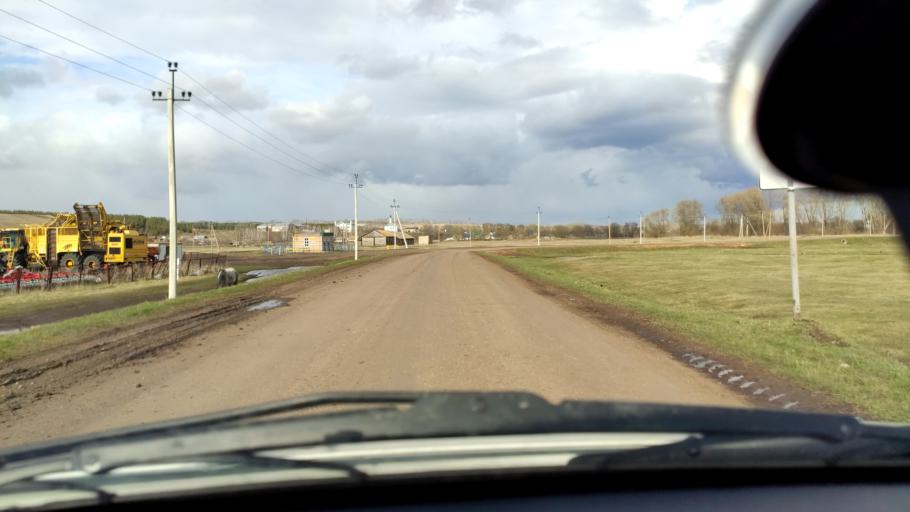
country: RU
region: Bashkortostan
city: Buzdyak
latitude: 54.7654
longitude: 54.6120
